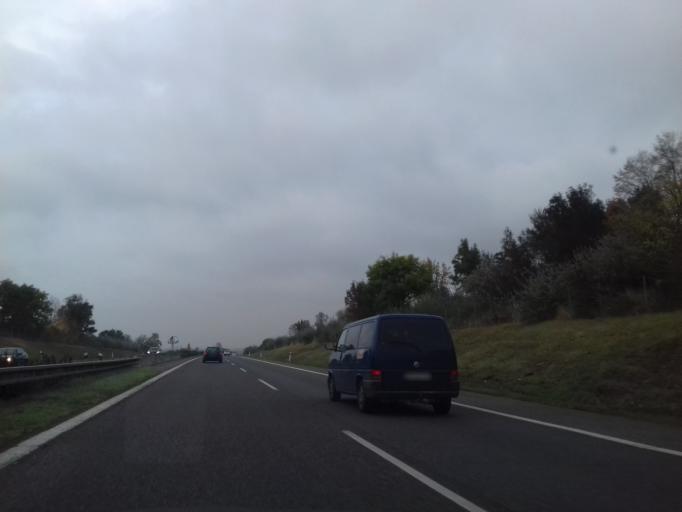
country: SK
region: Bratislavsky
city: Stupava
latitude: 48.2742
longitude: 17.0089
